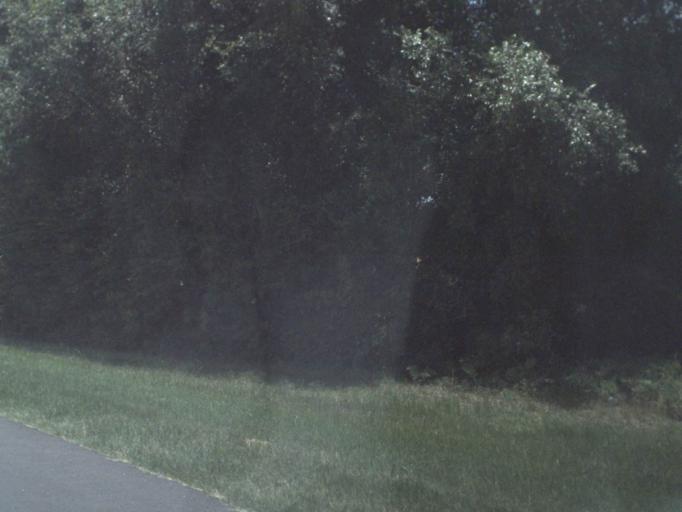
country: US
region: Florida
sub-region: Alachua County
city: Newberry
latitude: 29.6360
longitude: -82.6064
